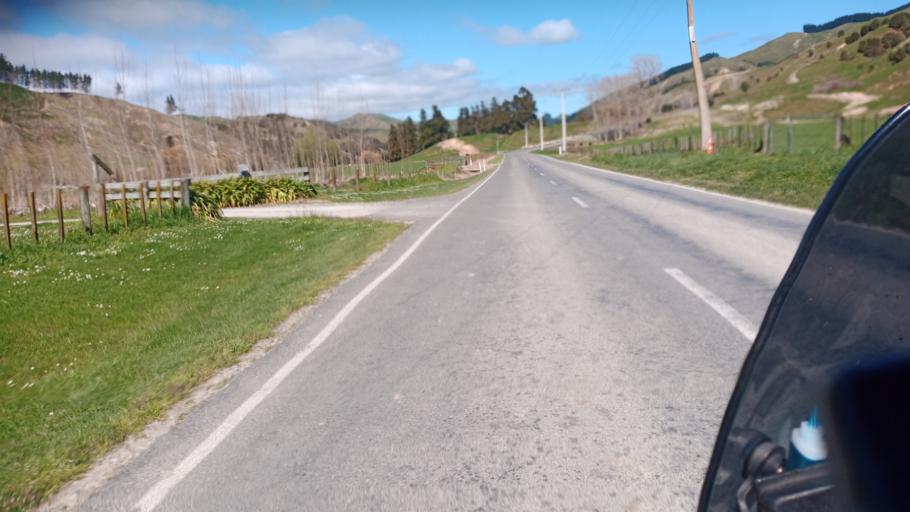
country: NZ
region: Gisborne
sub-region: Gisborne District
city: Gisborne
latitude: -38.7344
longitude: 177.8253
